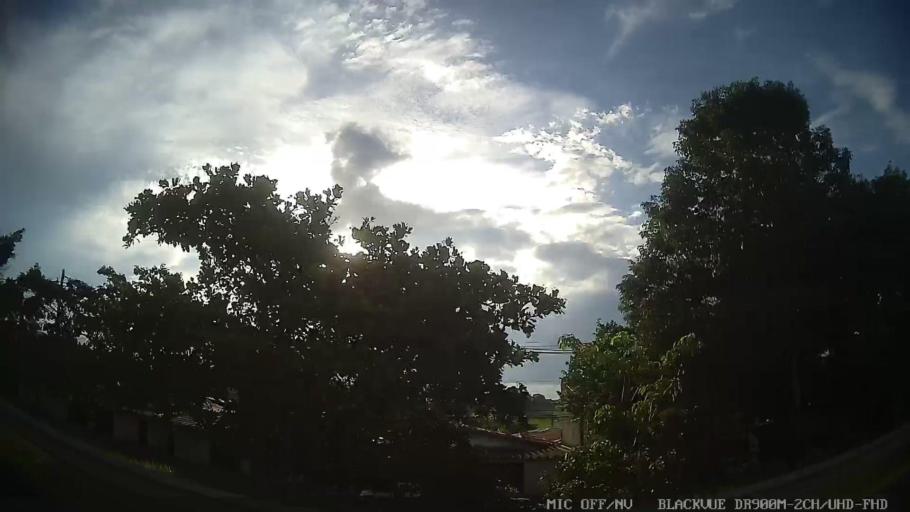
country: BR
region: Sao Paulo
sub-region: Tiete
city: Tiete
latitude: -23.1034
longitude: -47.7248
